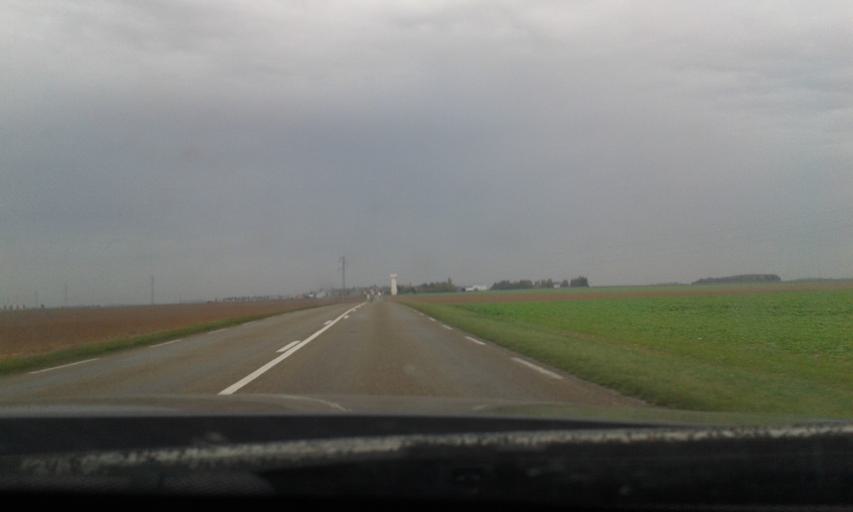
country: FR
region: Centre
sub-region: Departement d'Eure-et-Loir
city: Janville
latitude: 48.1927
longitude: 1.8286
